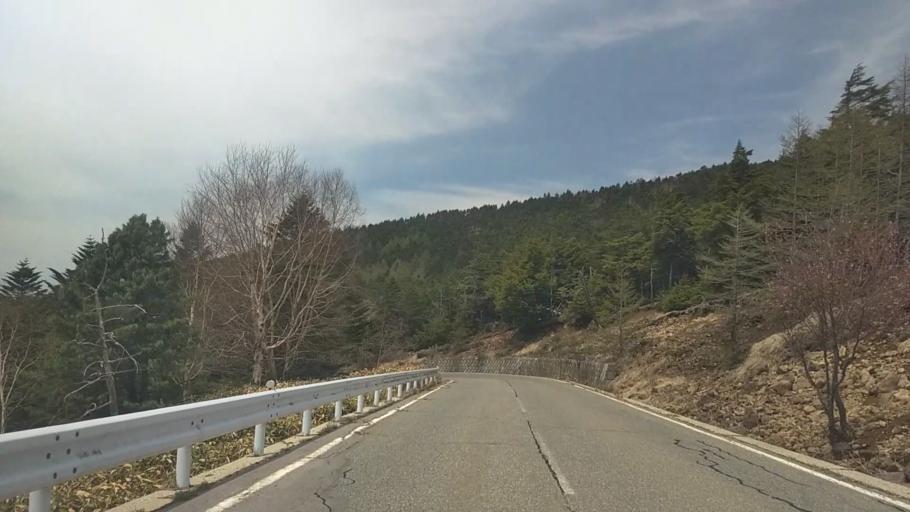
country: JP
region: Nagano
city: Chino
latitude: 36.0580
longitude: 138.3257
